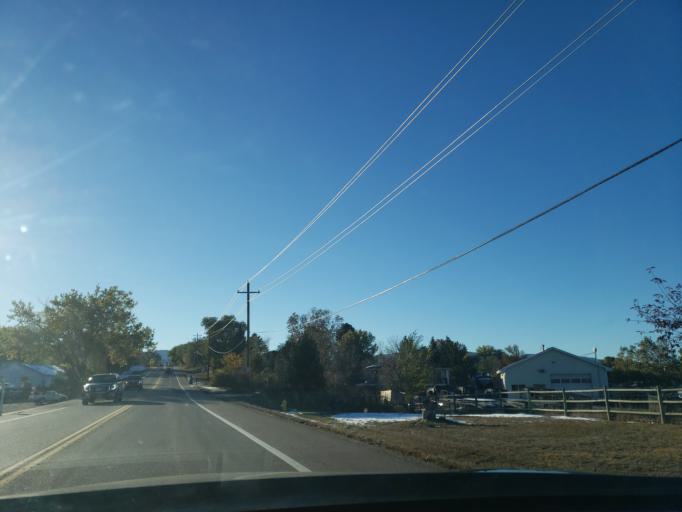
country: US
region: Colorado
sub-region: Larimer County
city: Fort Collins
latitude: 40.4948
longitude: -105.0723
